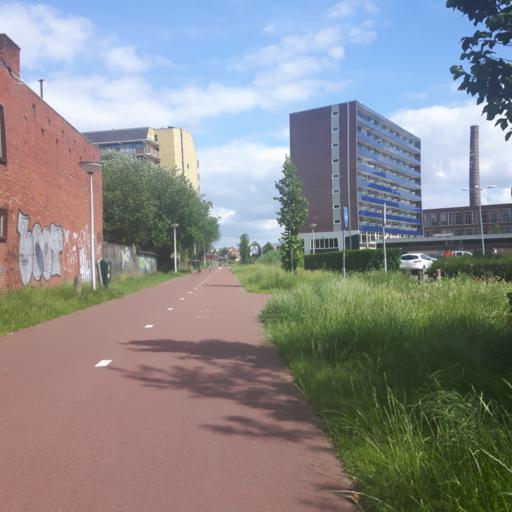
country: NL
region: Overijssel
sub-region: Gemeente Enschede
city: Enschede
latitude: 52.2151
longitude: 6.8851
